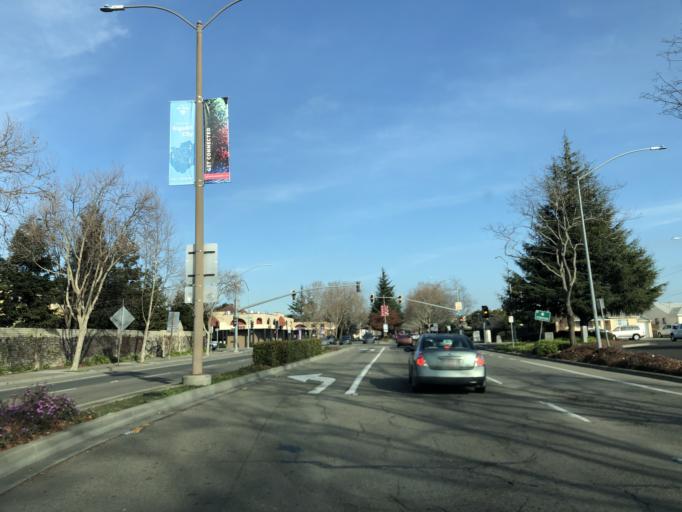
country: US
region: California
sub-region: Alameda County
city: San Leandro
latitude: 37.7208
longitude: -122.1715
